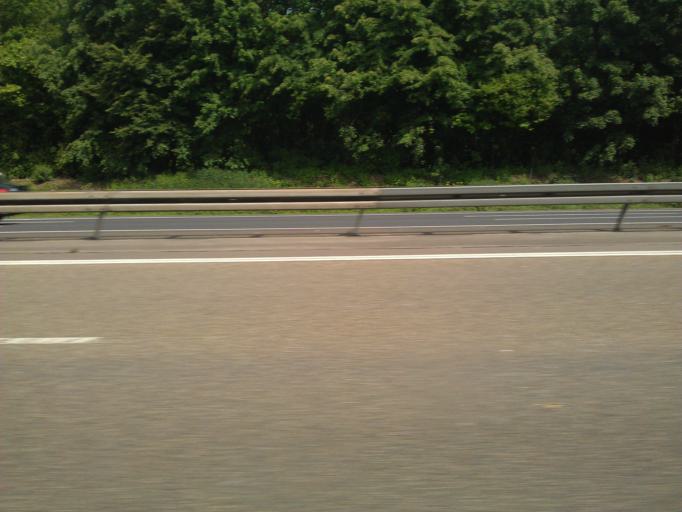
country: DE
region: North Rhine-Westphalia
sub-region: Regierungsbezirk Koln
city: Hurth
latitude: 50.8997
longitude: 6.9063
